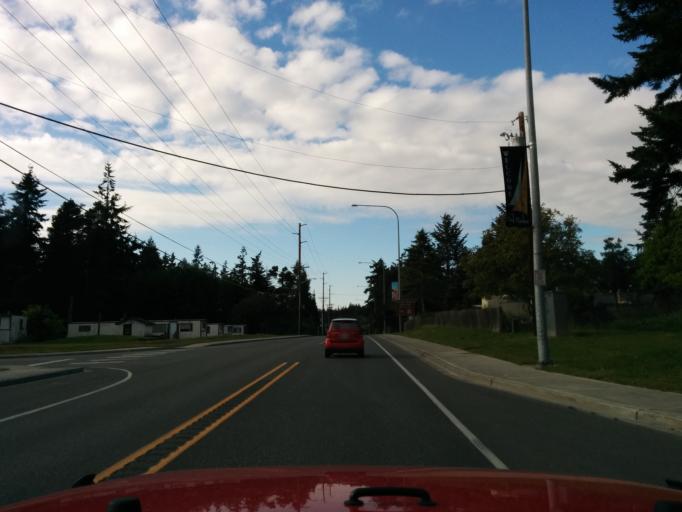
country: US
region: Washington
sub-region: Island County
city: Oak Harbor
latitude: 48.2787
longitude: -122.6695
